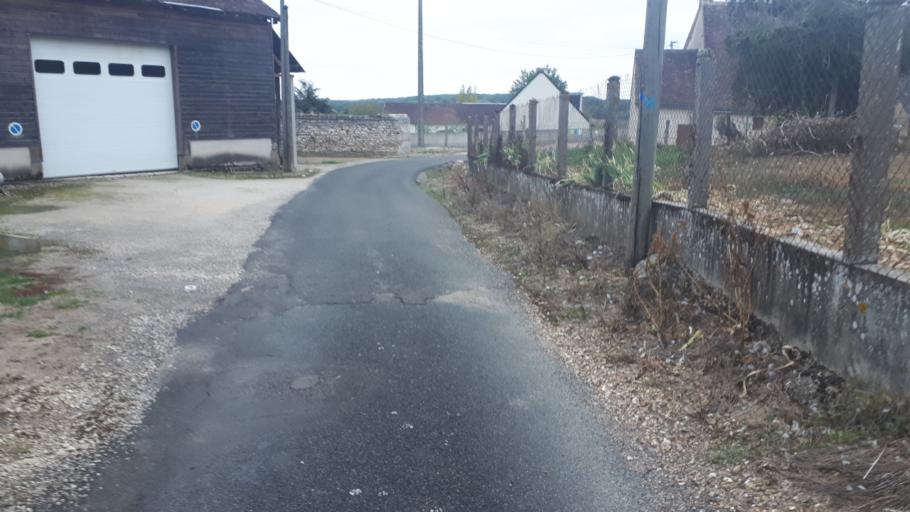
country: FR
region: Centre
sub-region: Departement du Loir-et-Cher
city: Villiers-sur-Loir
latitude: 47.8098
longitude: 0.9931
